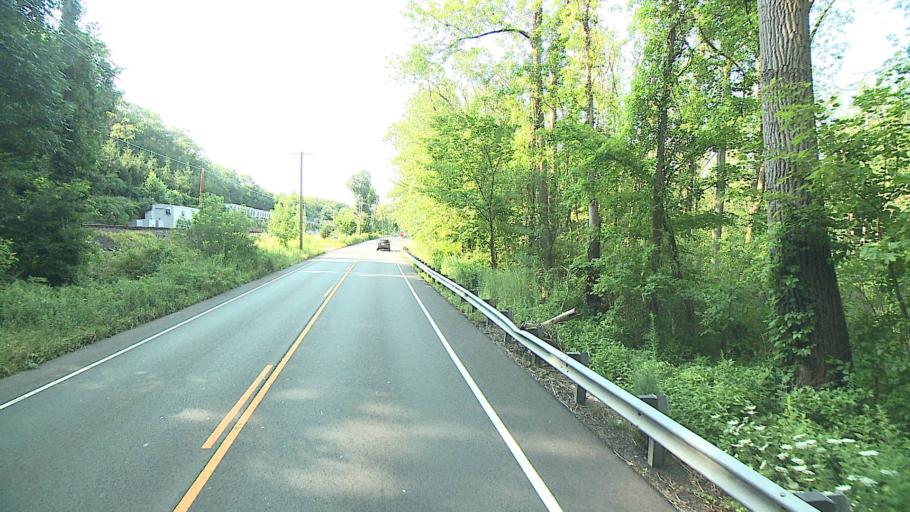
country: US
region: Connecticut
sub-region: Fairfield County
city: Georgetown
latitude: 41.2713
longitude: -73.4428
